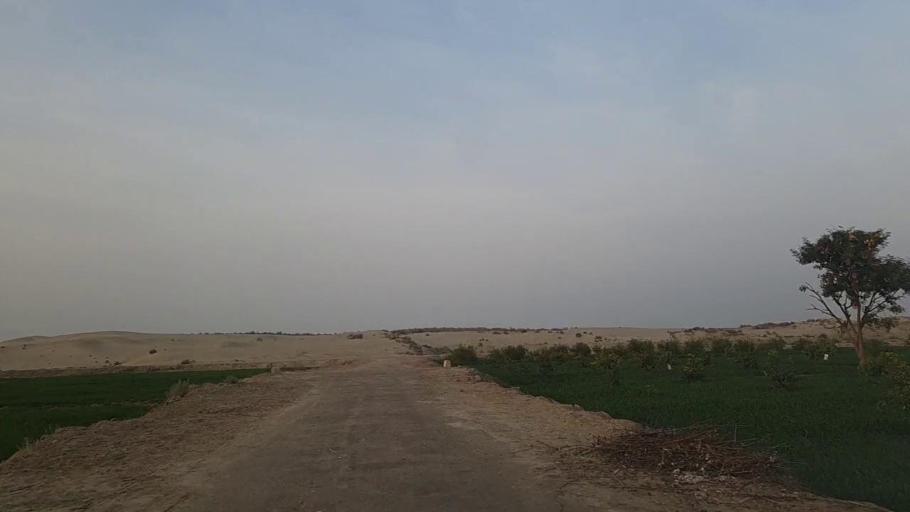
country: PK
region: Sindh
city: Jam Sahib
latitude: 26.4663
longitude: 68.5566
